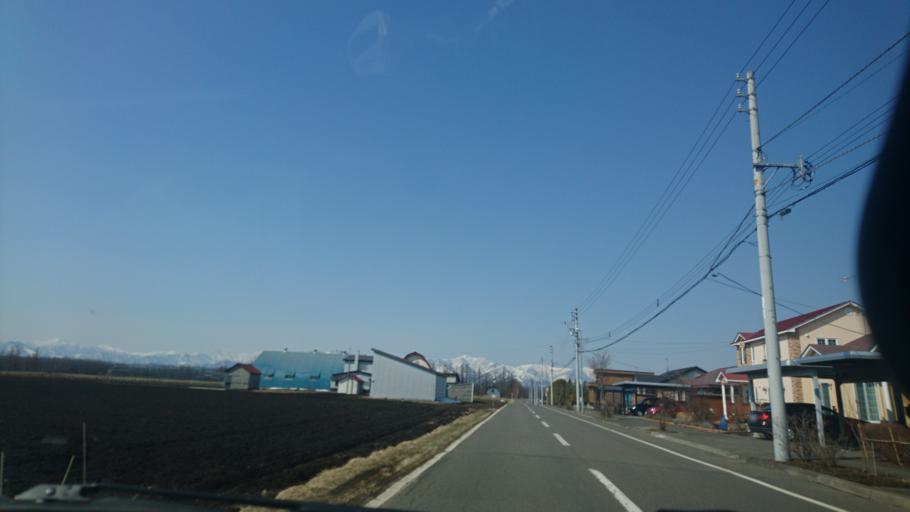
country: JP
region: Hokkaido
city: Obihiro
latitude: 42.9102
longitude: 143.0745
